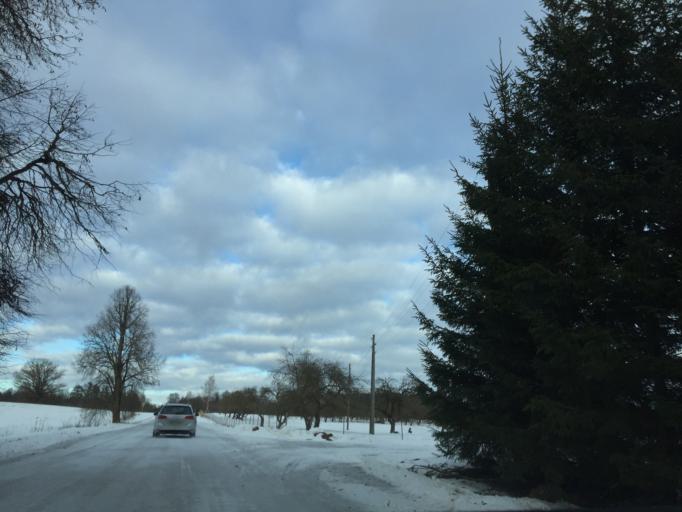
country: LV
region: Lielvarde
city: Lielvarde
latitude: 56.5661
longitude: 24.7339
